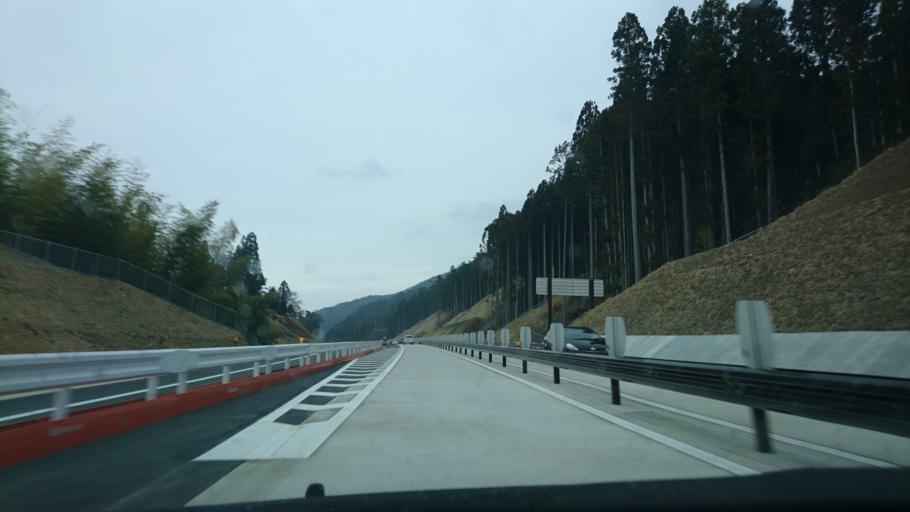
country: JP
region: Iwate
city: Ofunato
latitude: 38.9624
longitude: 141.6245
